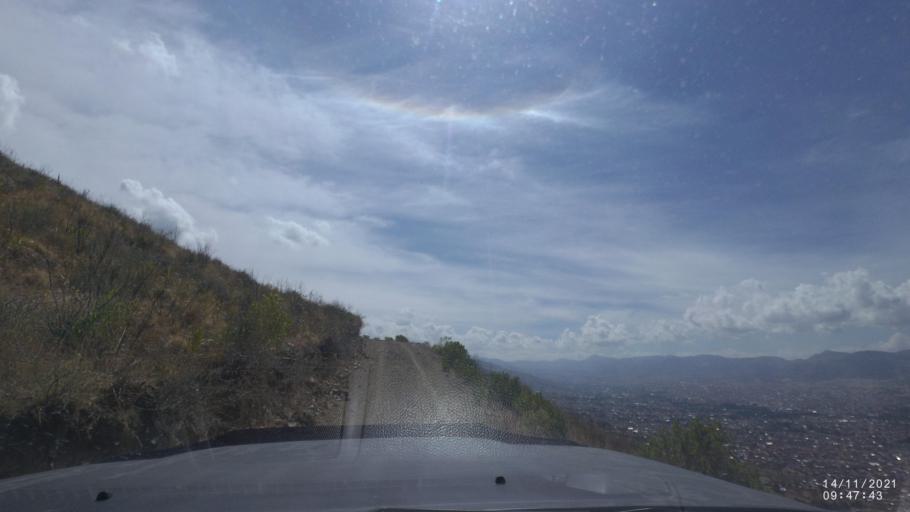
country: BO
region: Cochabamba
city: Cochabamba
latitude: -17.3626
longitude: -66.0887
